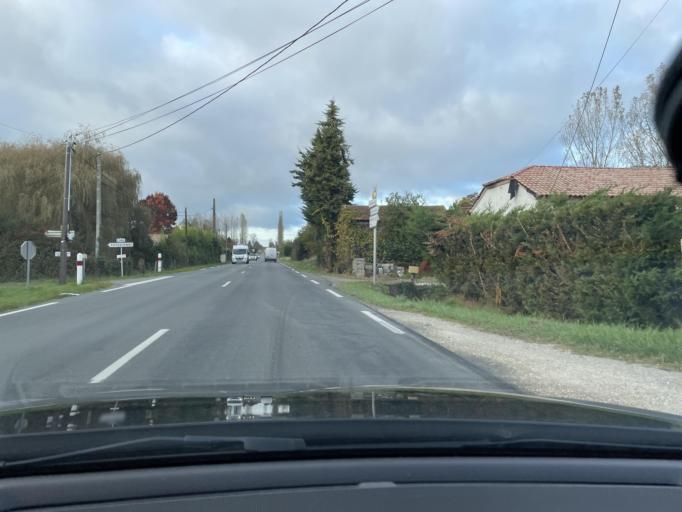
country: FR
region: Aquitaine
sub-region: Departement du Lot-et-Garonne
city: Casteljaloux
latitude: 44.3506
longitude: 0.1073
